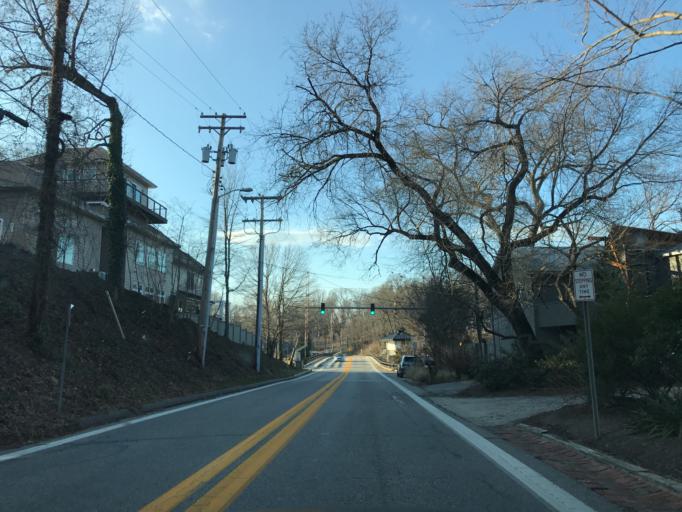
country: US
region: Maryland
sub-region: Anne Arundel County
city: Annapolis
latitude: 38.9919
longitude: -76.5067
